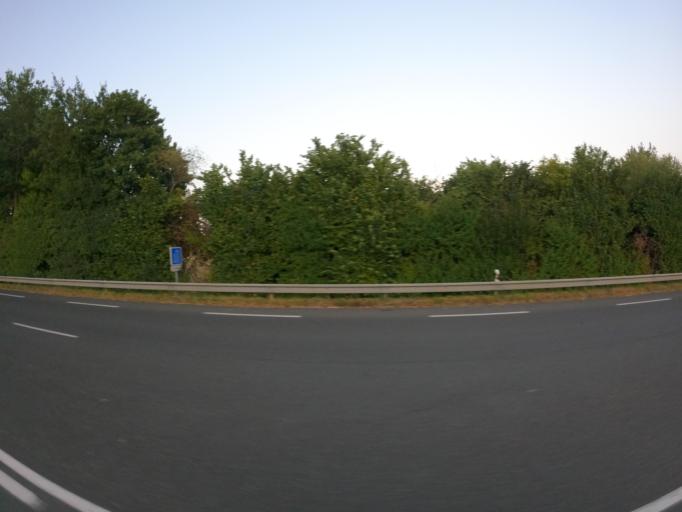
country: FR
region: Pays de la Loire
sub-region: Departement de Maine-et-Loire
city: Segre
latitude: 47.6792
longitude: -0.8588
